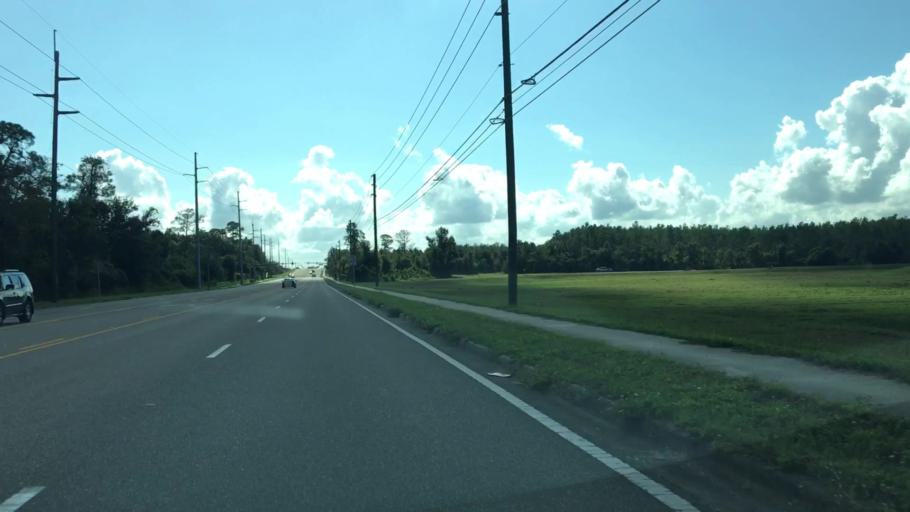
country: US
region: Florida
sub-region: Volusia County
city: Deltona
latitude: 28.8932
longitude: -81.2827
